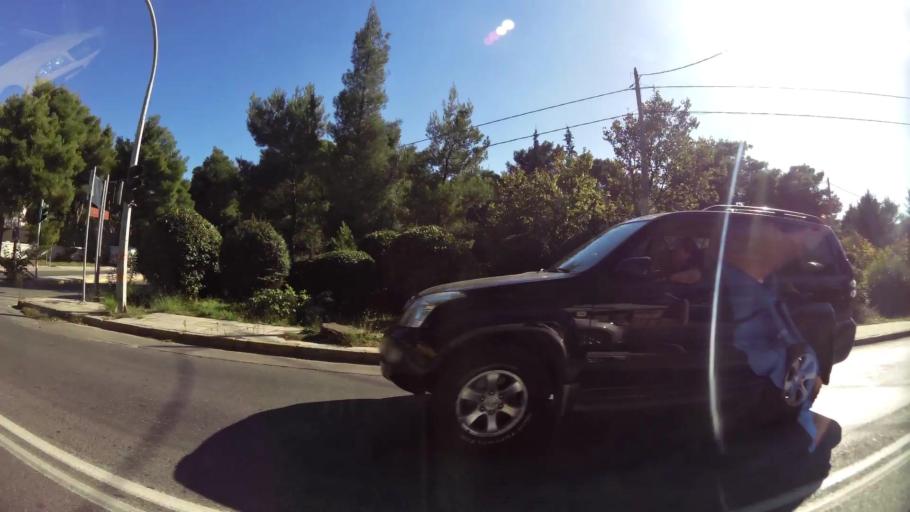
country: GR
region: Attica
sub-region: Nomarchia Anatolikis Attikis
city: Drosia
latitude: 38.1144
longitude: 23.8501
